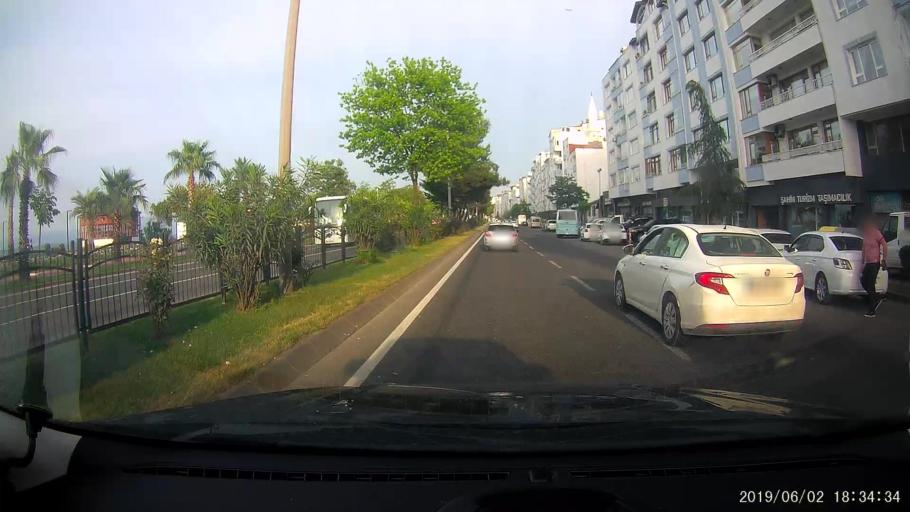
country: TR
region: Ordu
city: Fatsa
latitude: 41.0289
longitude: 37.5058
